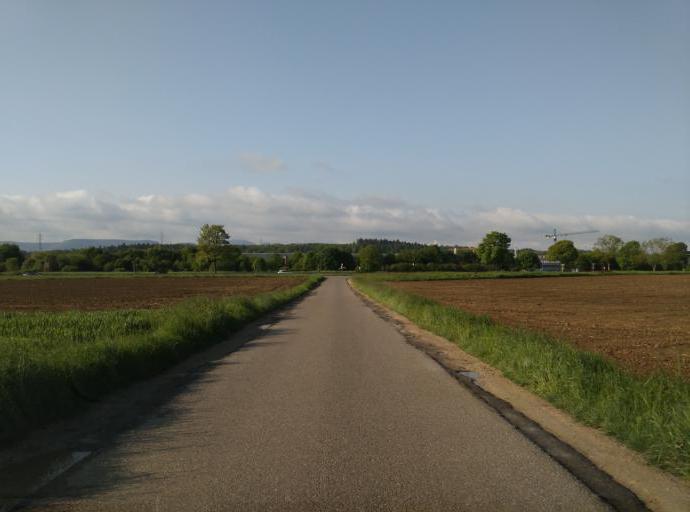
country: DE
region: Baden-Wuerttemberg
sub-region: Tuebingen Region
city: Wannweil
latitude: 48.5000
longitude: 9.1435
